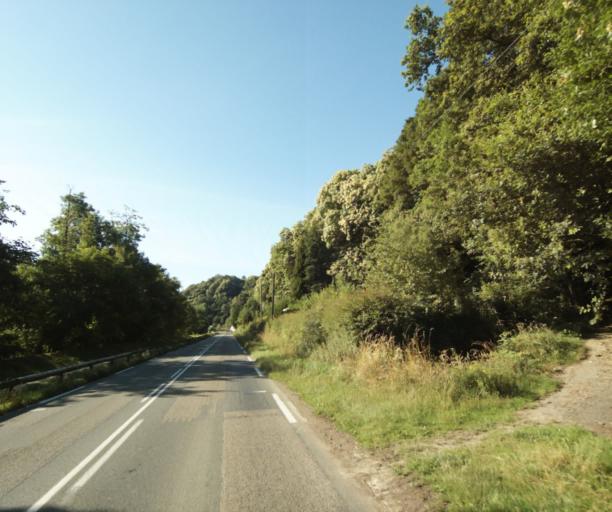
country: FR
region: Pays de la Loire
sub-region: Departement de la Mayenne
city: Laval
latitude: 48.0411
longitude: -0.7650
